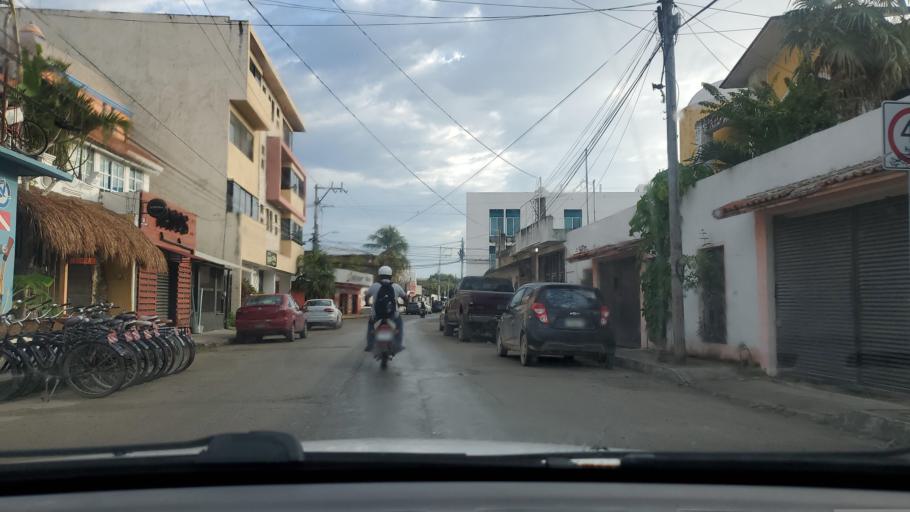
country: MX
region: Quintana Roo
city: Tulum
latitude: 20.2124
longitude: -87.4615
